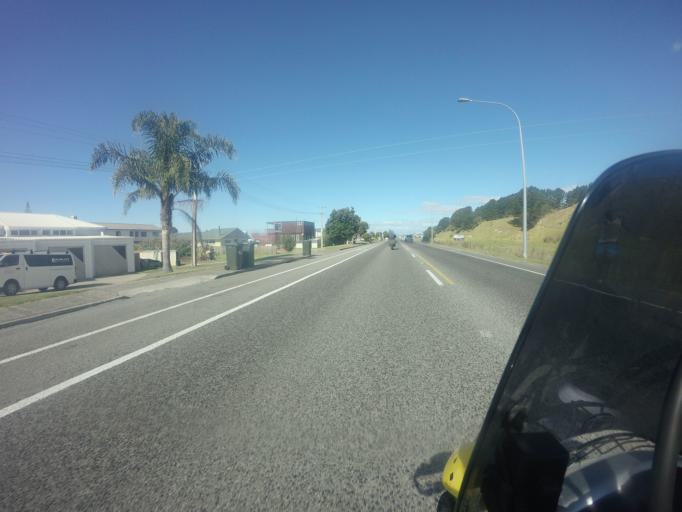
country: NZ
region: Bay of Plenty
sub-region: Whakatane District
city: Whakatane
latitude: -37.9727
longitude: 177.0606
